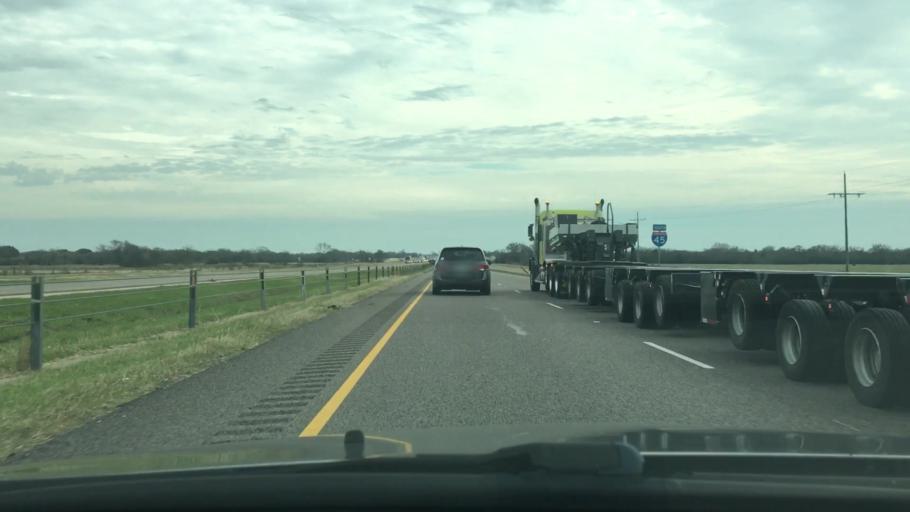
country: US
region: Texas
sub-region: Madison County
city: Madisonville
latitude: 31.0077
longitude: -95.9182
